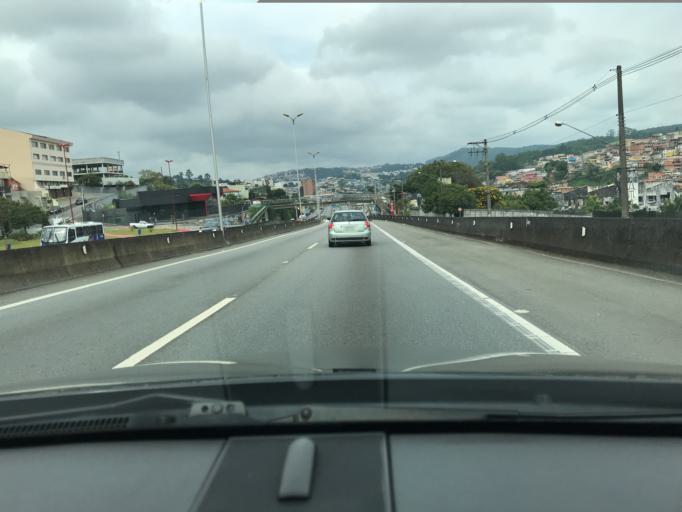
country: BR
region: Sao Paulo
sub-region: Cotia
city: Cotia
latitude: -23.6009
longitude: -46.9061
